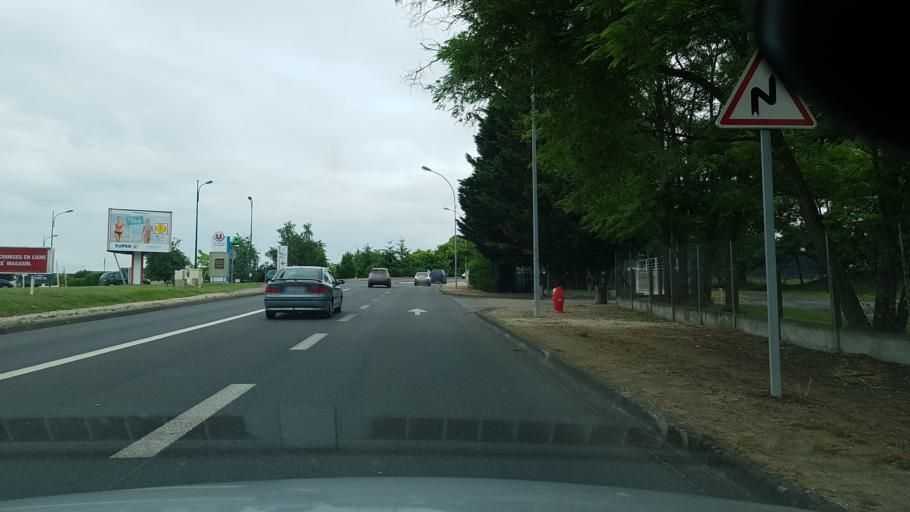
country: FR
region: Centre
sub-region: Departement du Loir-et-Cher
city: Selles-sur-Cher
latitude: 47.2837
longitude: 1.5411
